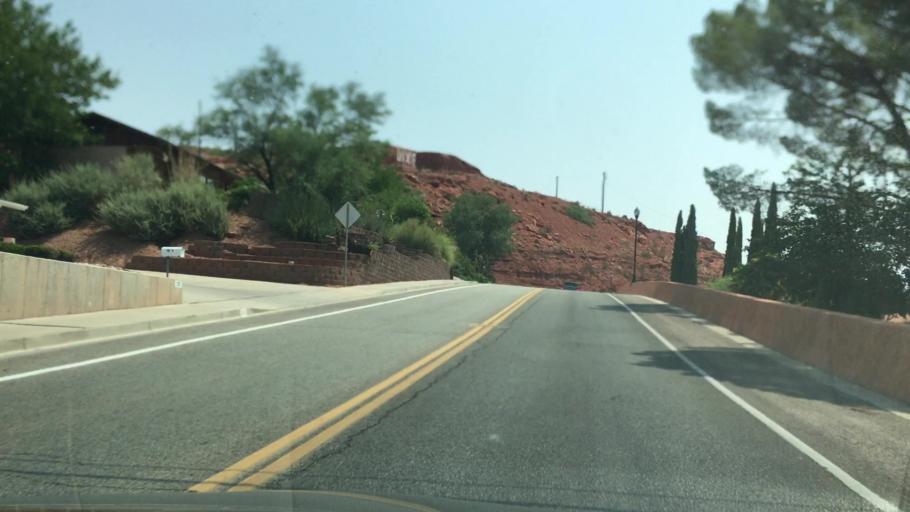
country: US
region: Utah
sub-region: Washington County
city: Saint George
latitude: 37.1151
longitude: -113.5828
